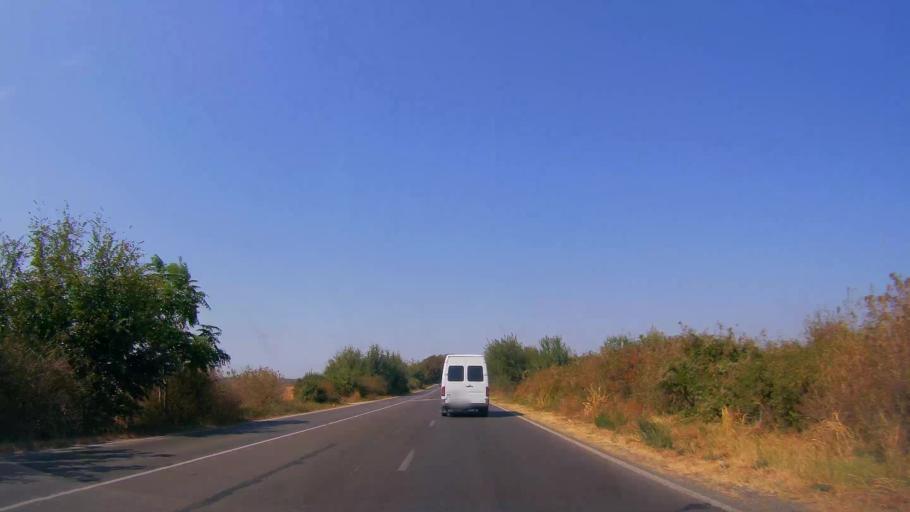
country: BG
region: Razgrad
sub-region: Obshtina Tsar Kaloyan
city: Tsar Kaloyan
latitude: 43.6298
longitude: 26.2044
